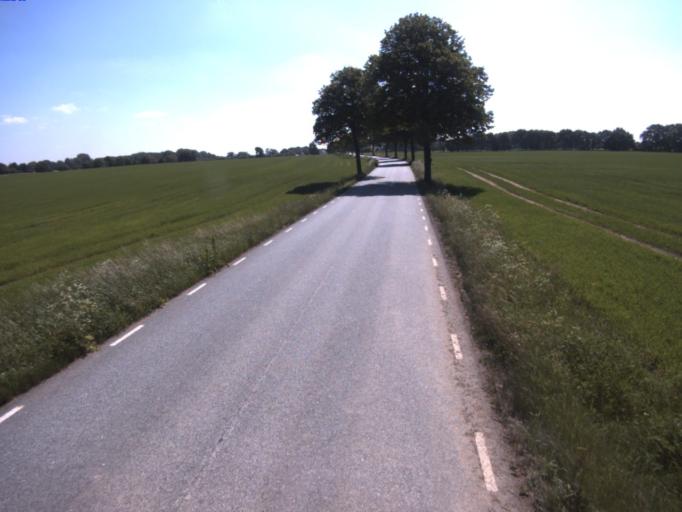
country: SE
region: Skane
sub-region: Helsingborg
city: Odakra
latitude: 56.1123
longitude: 12.6747
